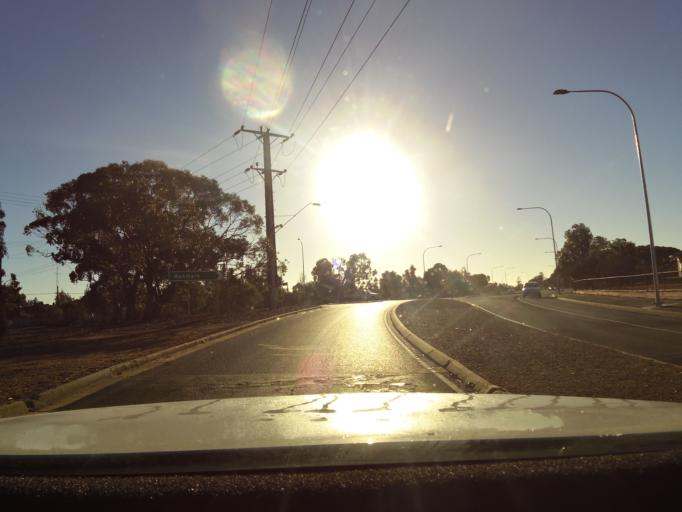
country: AU
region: South Australia
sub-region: Berri and Barmera
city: Berri
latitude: -34.2823
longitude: 140.5973
